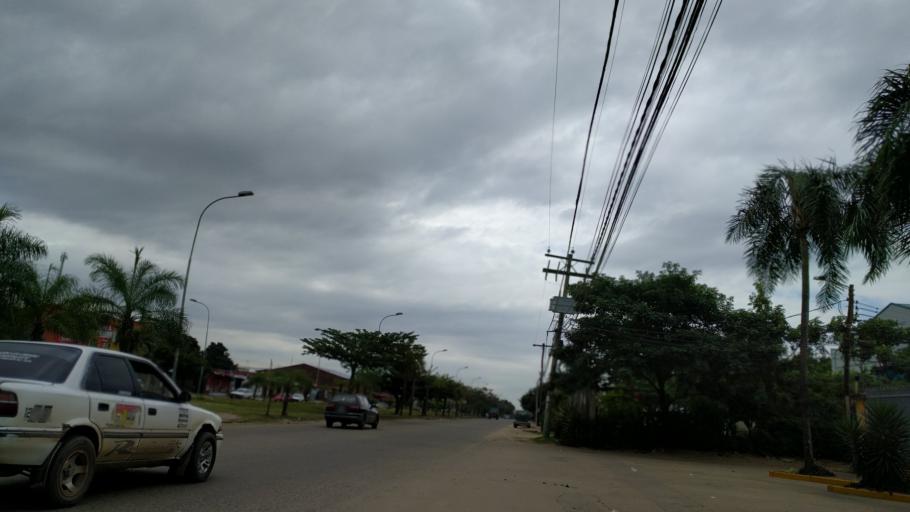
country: BO
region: Santa Cruz
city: Santa Cruz de la Sierra
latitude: -17.8165
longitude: -63.2244
